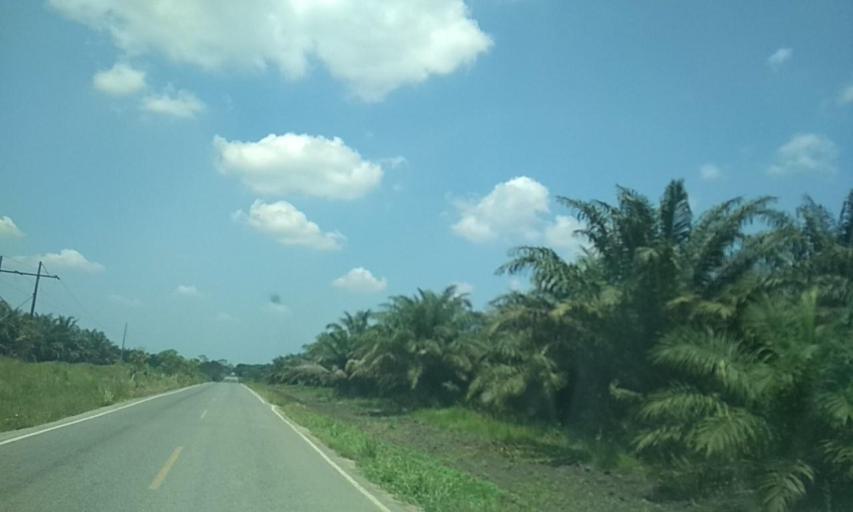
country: MX
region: Tabasco
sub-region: Huimanguillo
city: Paso de la Mina 2da. Seccion (Barrial)
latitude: 17.7559
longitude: -93.6612
